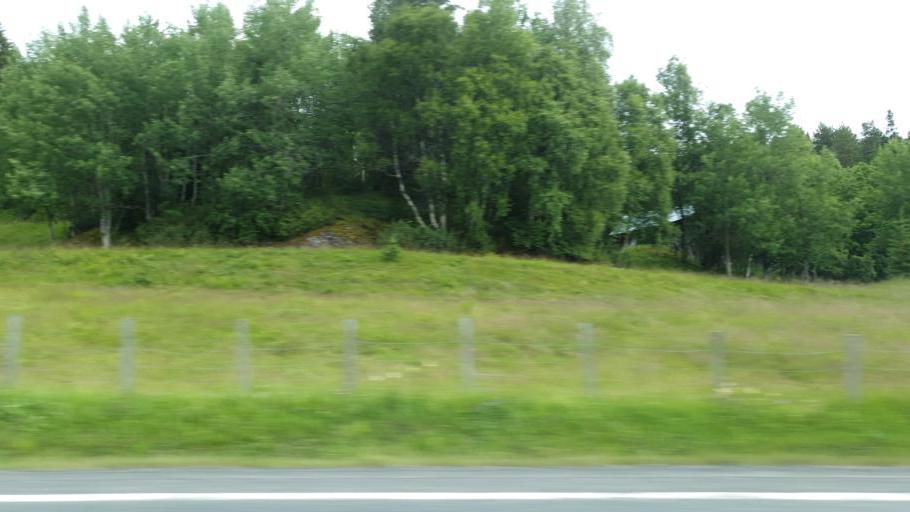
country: NO
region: Sor-Trondelag
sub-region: Rennebu
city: Berkak
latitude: 62.8703
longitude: 10.0389
